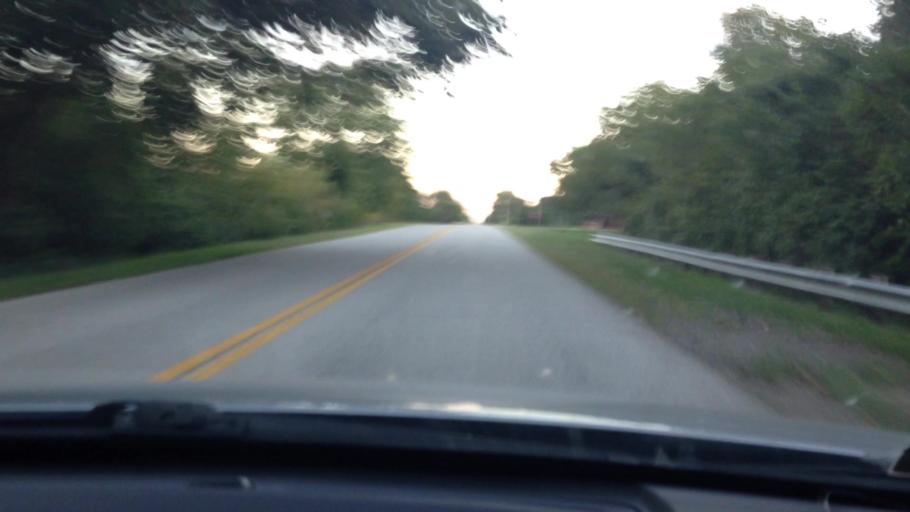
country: US
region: Kansas
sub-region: Leavenworth County
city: Lansing
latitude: 39.1823
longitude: -94.8267
